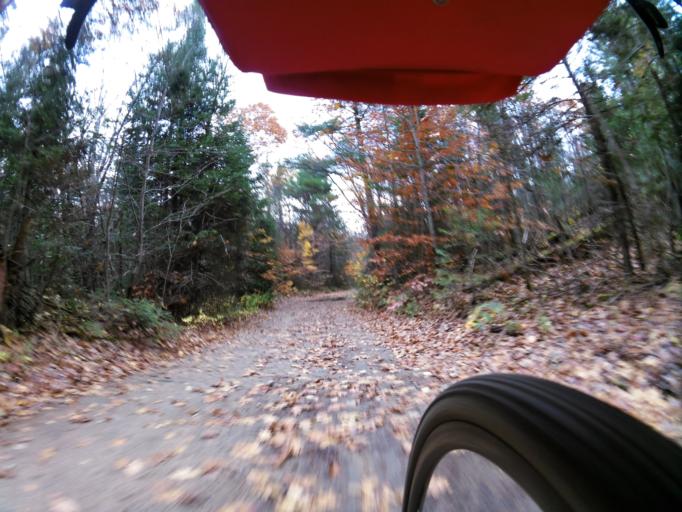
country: CA
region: Ontario
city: Arnprior
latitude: 45.6584
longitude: -76.2111
